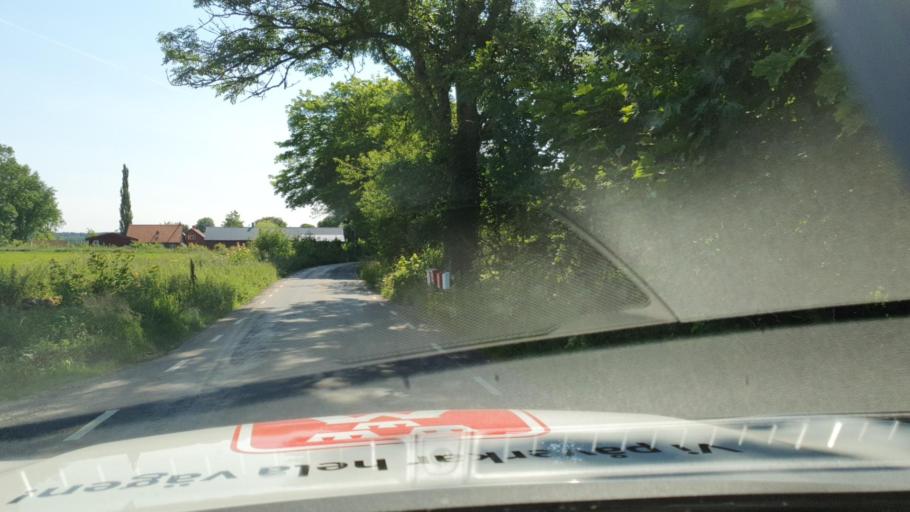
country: SE
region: Vaestra Goetaland
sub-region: Skovde Kommun
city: Stopen
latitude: 58.5032
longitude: 13.7763
